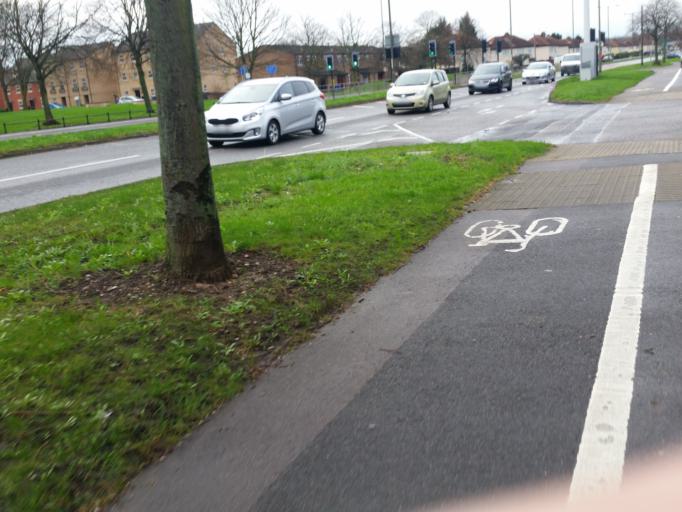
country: GB
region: England
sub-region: Derby
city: Derby
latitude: 52.8923
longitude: -1.4447
